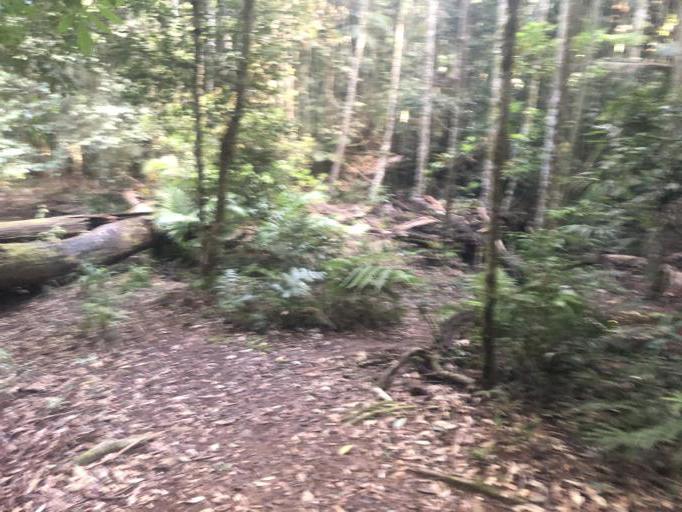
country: AU
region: New South Wales
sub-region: Coffs Harbour
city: Coffs Harbour
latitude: -30.2417
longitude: 153.0956
